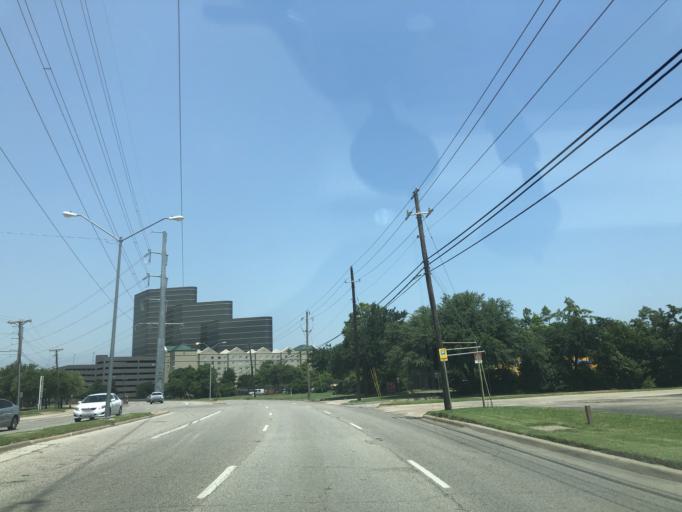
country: US
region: Texas
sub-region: Dallas County
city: Dallas
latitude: 32.8068
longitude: -96.8459
